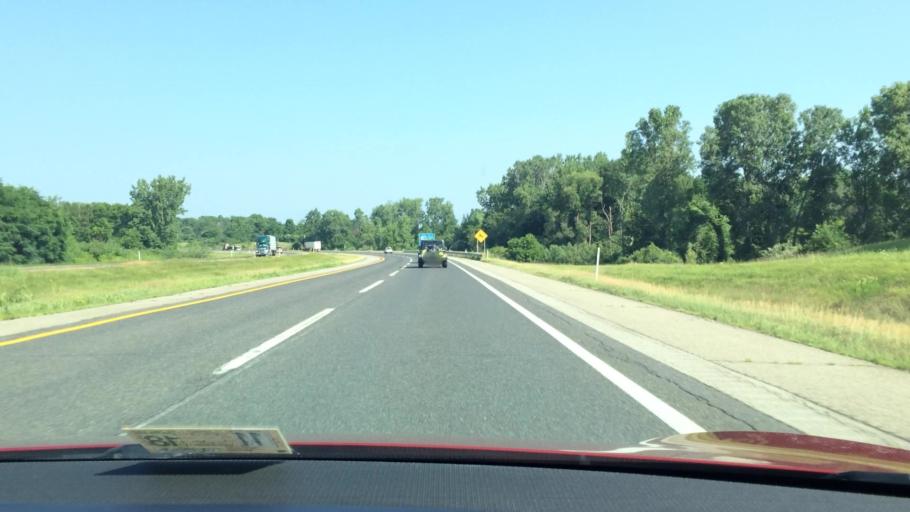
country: US
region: Indiana
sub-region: Steuben County
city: Fremont
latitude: 41.7321
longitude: -84.9724
